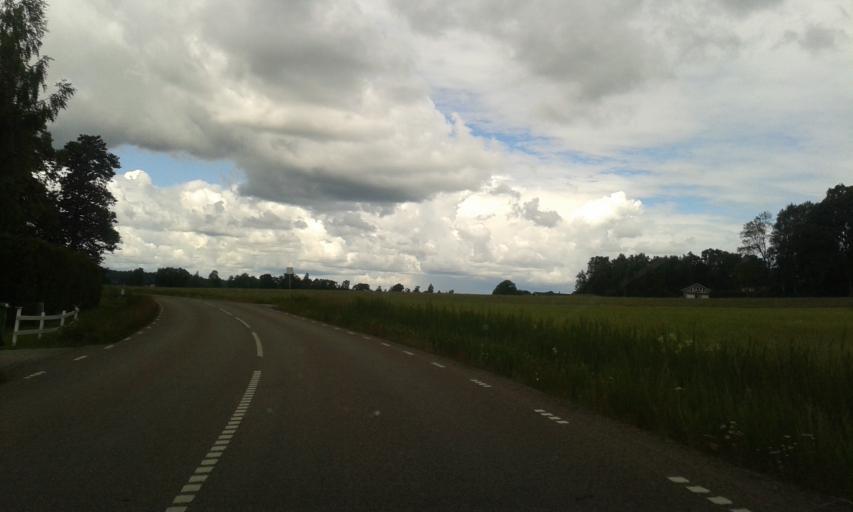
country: SE
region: Vaestra Goetaland
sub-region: Lilla Edets Kommun
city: Lilla Edet
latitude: 58.1171
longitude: 12.1162
